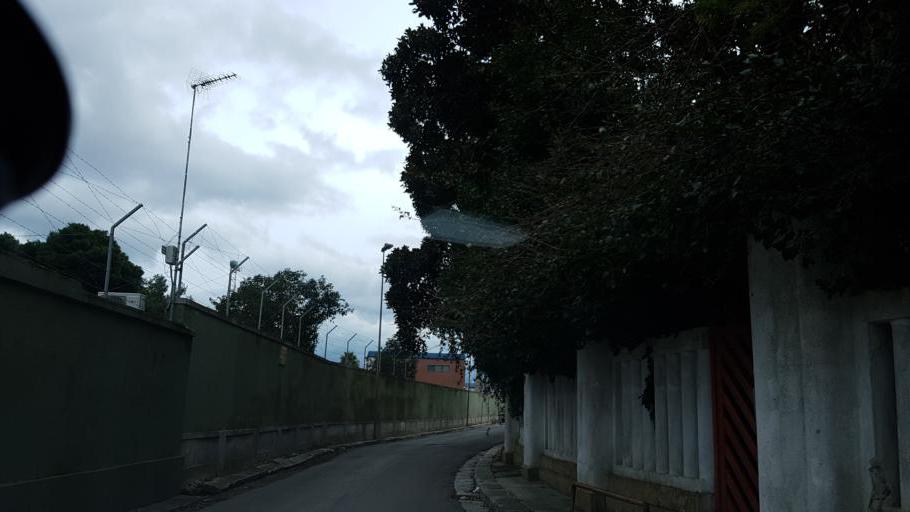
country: IT
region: Apulia
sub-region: Provincia di Brindisi
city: Materdomini
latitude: 40.6494
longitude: 17.9467
